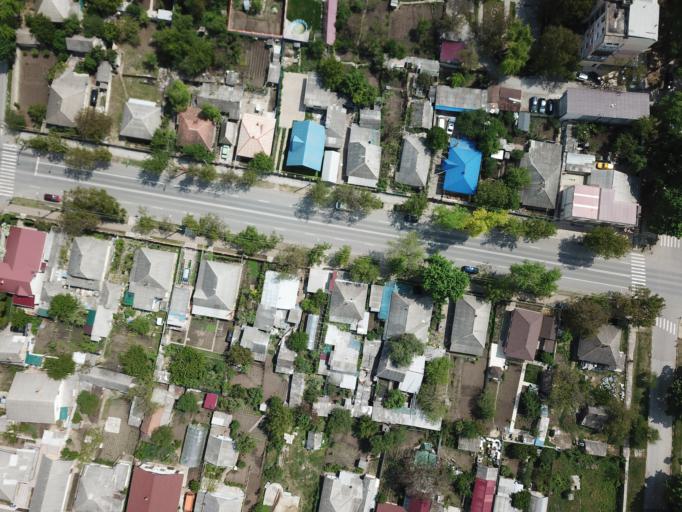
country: MD
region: Ungheni
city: Ungheni
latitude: 47.2141
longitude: 27.8024
